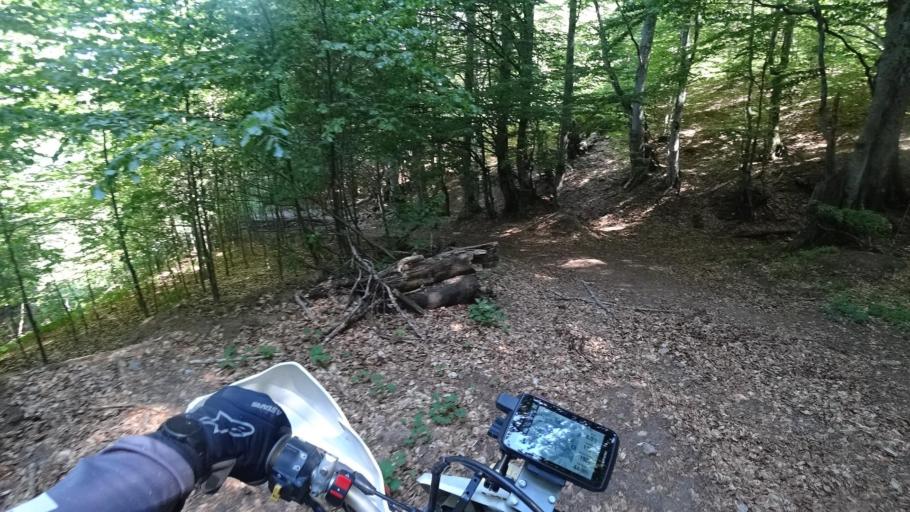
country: HR
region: Zadarska
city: Gracac
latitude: 44.4218
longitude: 15.9941
